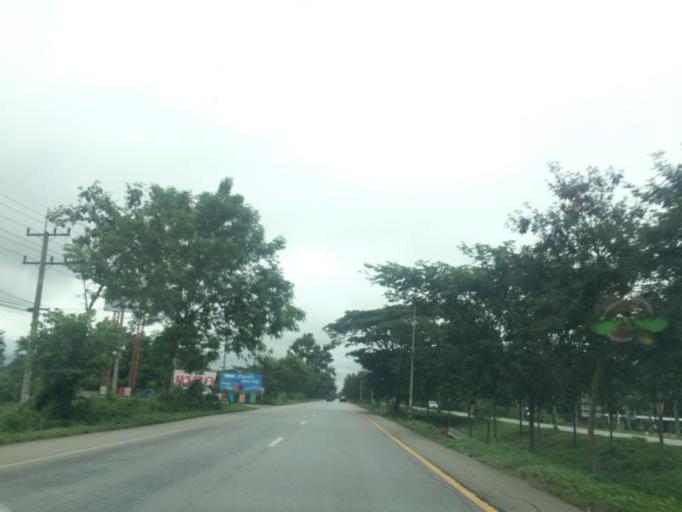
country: TH
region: Chiang Rai
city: Mae Lao
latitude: 19.7882
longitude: 99.7465
